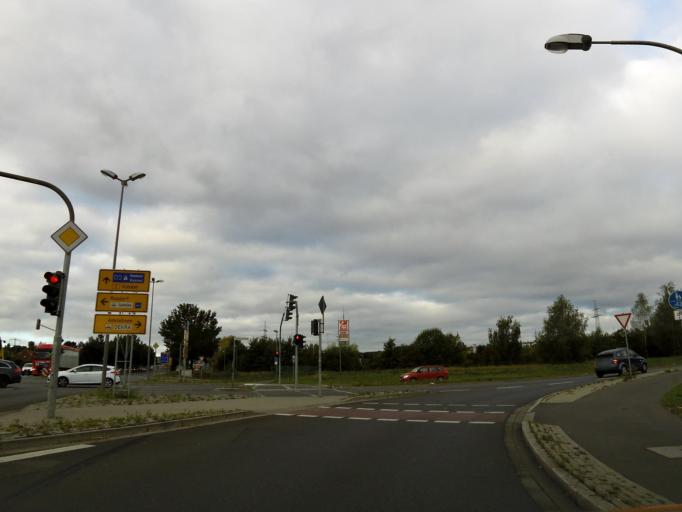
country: DE
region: Lower Saxony
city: Rosdorf
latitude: 51.5276
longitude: 9.8870
